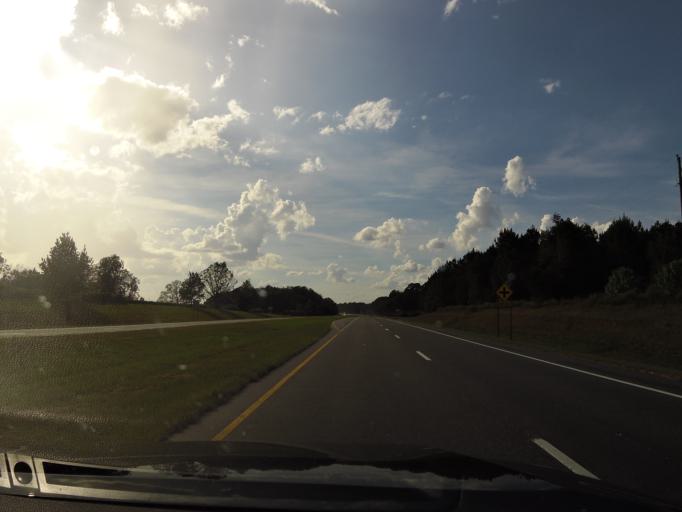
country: US
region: Georgia
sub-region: Brooks County
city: Quitman
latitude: 30.7876
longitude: -83.6330
